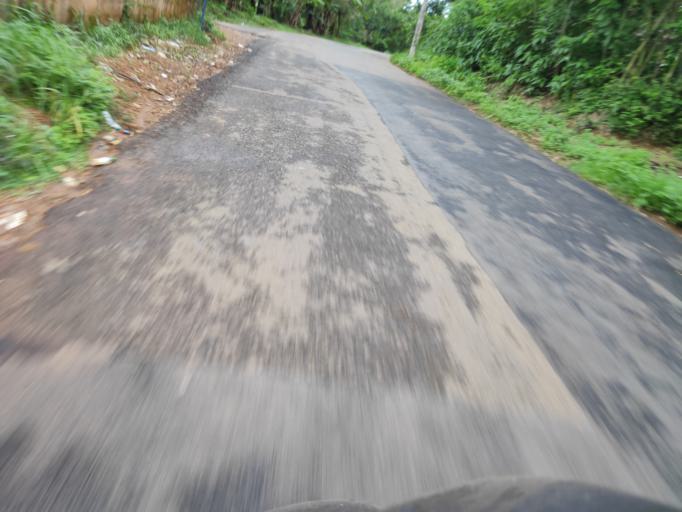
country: IN
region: Kerala
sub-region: Malappuram
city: Manjeri
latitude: 11.1789
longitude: 76.1958
